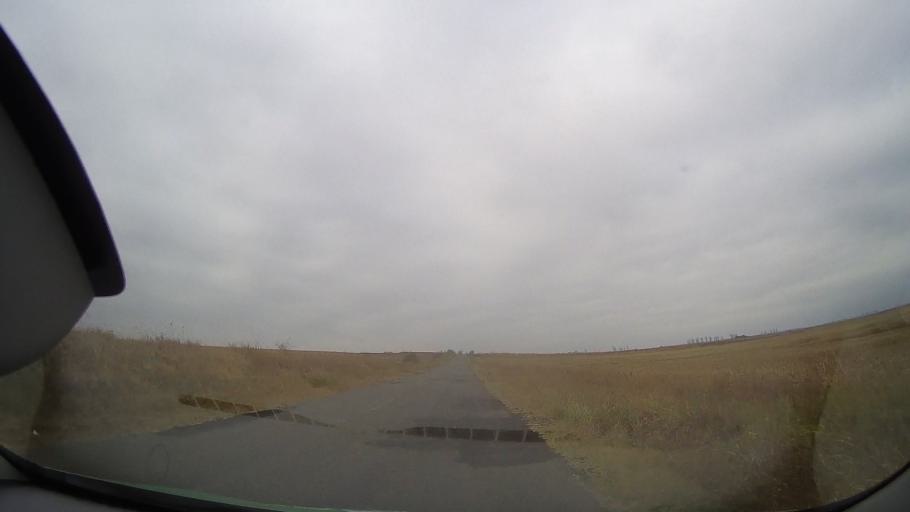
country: RO
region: Buzau
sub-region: Comuna Luciu
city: Luciu
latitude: 44.9772
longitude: 27.0561
